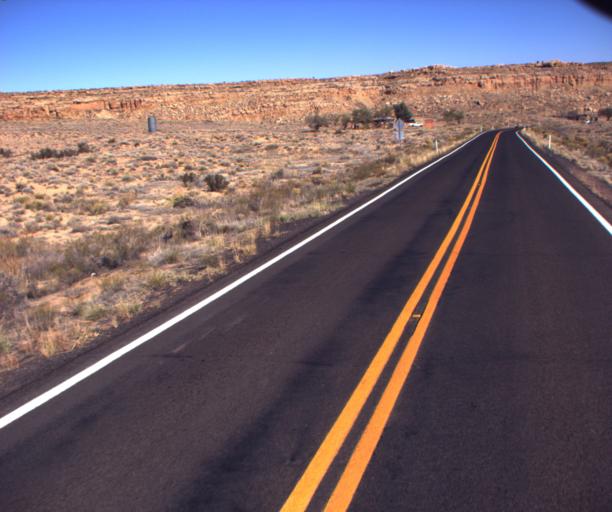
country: US
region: Arizona
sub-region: Navajo County
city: First Mesa
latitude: 35.8809
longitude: -110.6237
